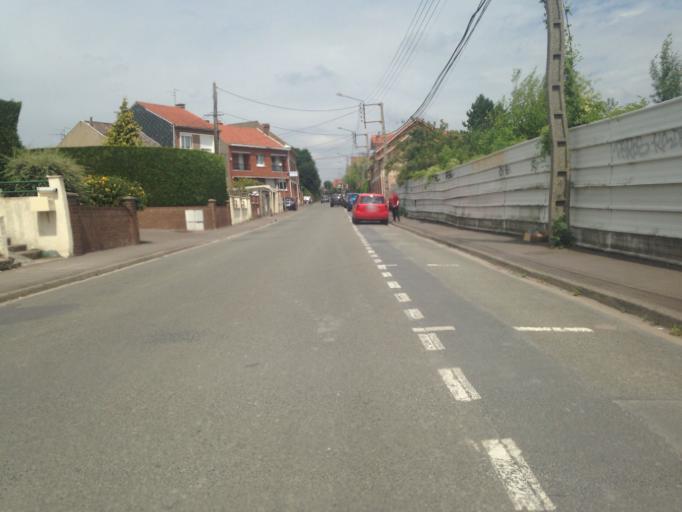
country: FR
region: Nord-Pas-de-Calais
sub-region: Departement du Pas-de-Calais
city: Lens
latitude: 50.4369
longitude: 2.8299
